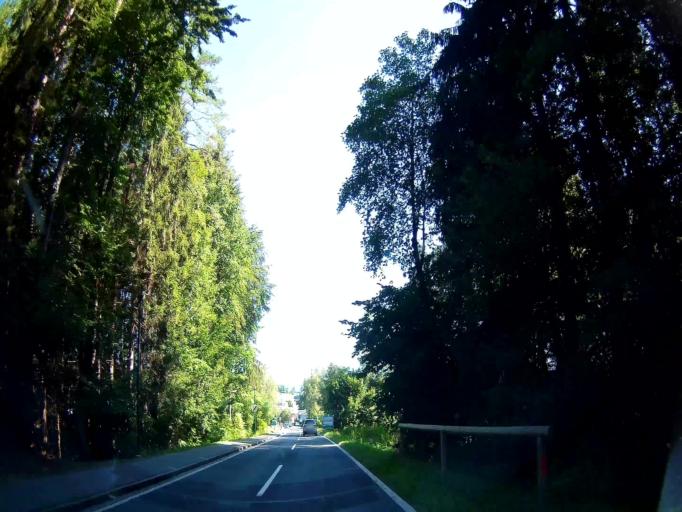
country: AT
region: Carinthia
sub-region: Politischer Bezirk Volkermarkt
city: Eberndorf
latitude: 46.6110
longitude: 14.5759
